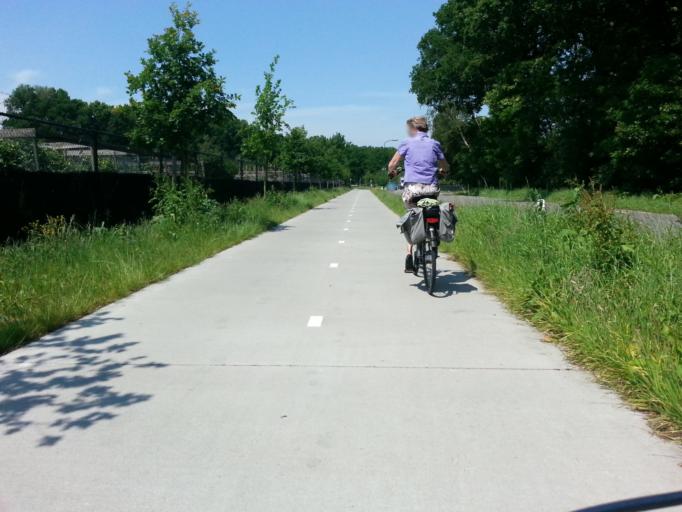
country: NL
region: Utrecht
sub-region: Gemeente Leusden
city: Leusden
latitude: 52.1340
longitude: 5.4485
